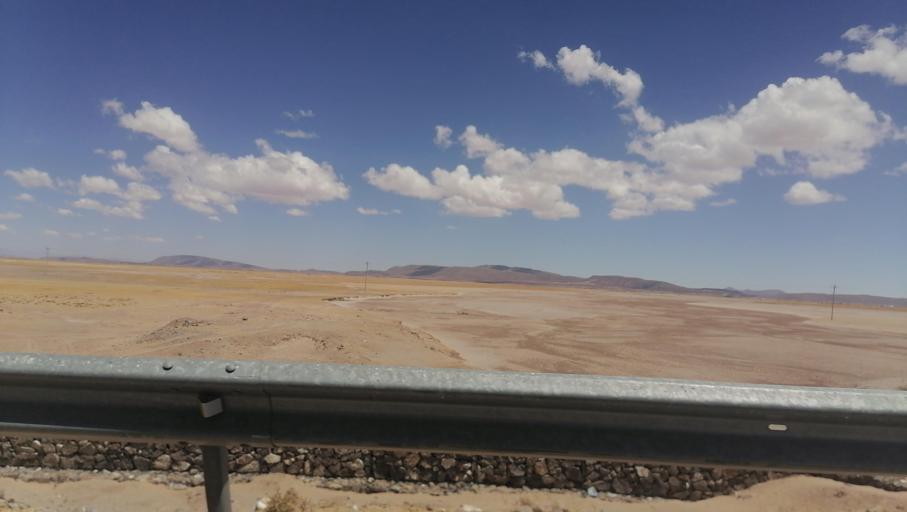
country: BO
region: Oruro
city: Challapata
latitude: -19.2135
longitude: -67.0240
